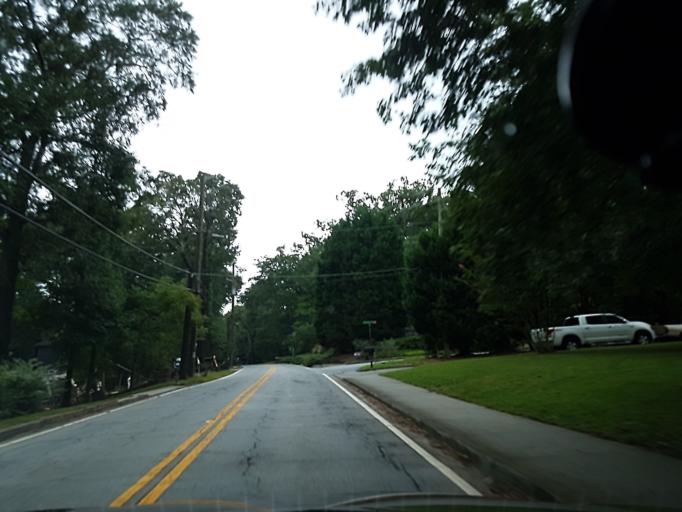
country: US
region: Georgia
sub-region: DeKalb County
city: North Druid Hills
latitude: 33.8115
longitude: -84.3205
